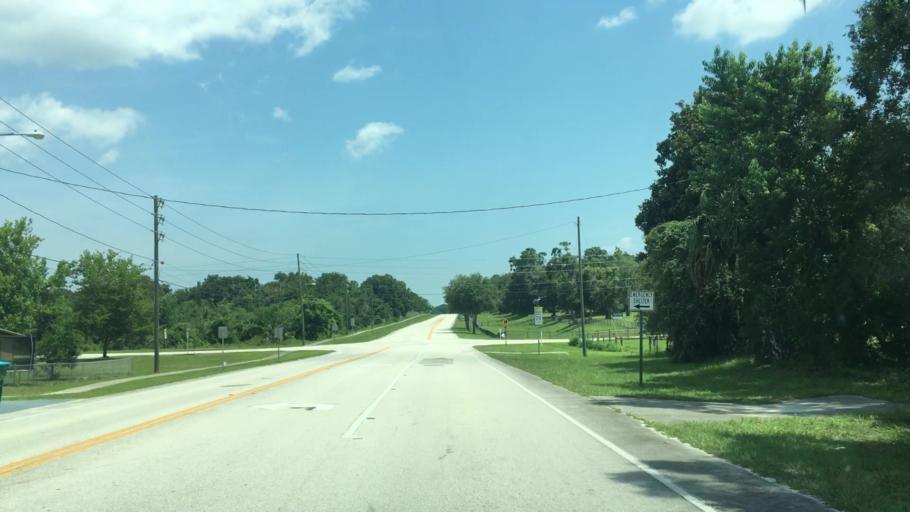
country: US
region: Florida
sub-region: Volusia County
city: Lake Helen
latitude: 28.9693
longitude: -81.2236
